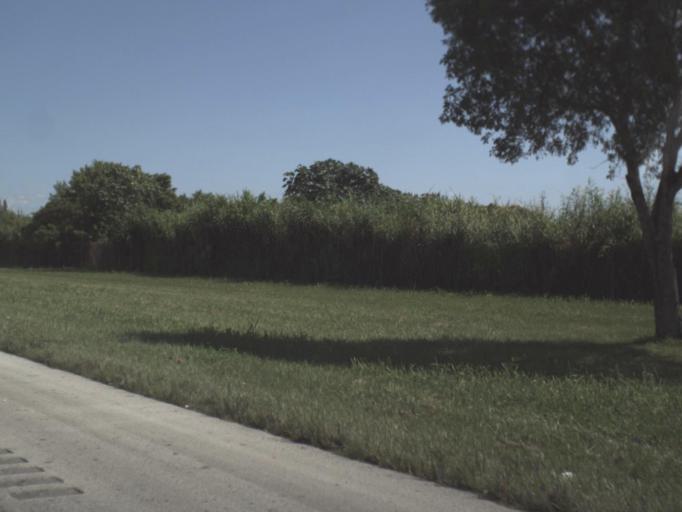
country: US
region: Florida
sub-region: Miami-Dade County
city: Naranja
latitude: 25.5143
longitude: -80.4081
